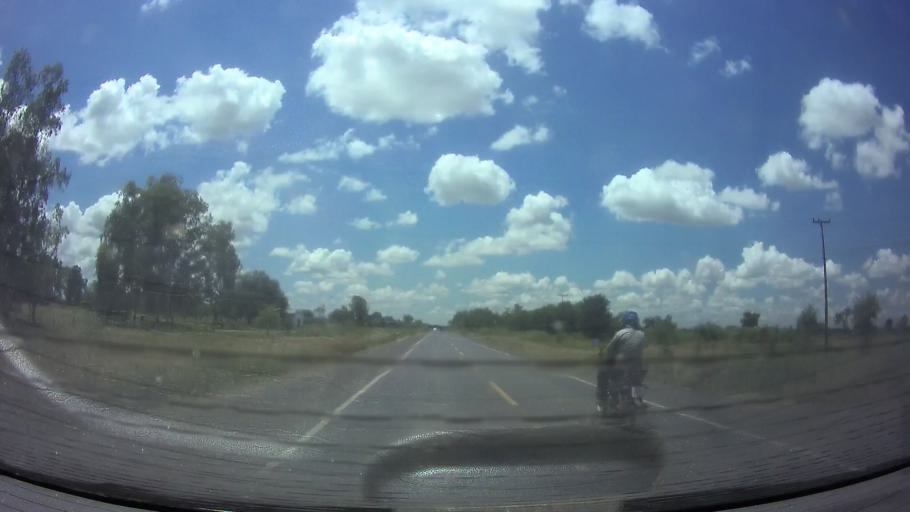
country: PY
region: Presidente Hayes
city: Nanawa
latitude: -25.2172
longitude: -57.6702
